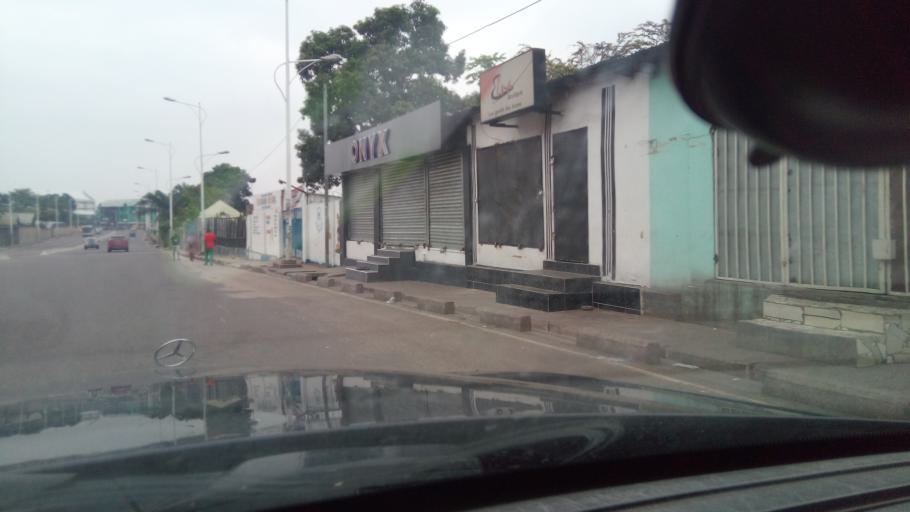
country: CD
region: Kinshasa
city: Kinshasa
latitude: -4.3335
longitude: 15.2589
